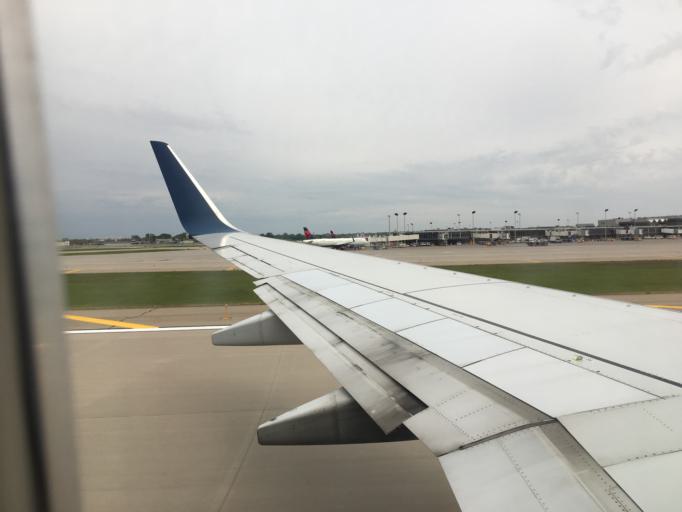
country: US
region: Minnesota
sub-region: Hennepin County
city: Richfield
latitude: 44.8871
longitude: -93.2325
